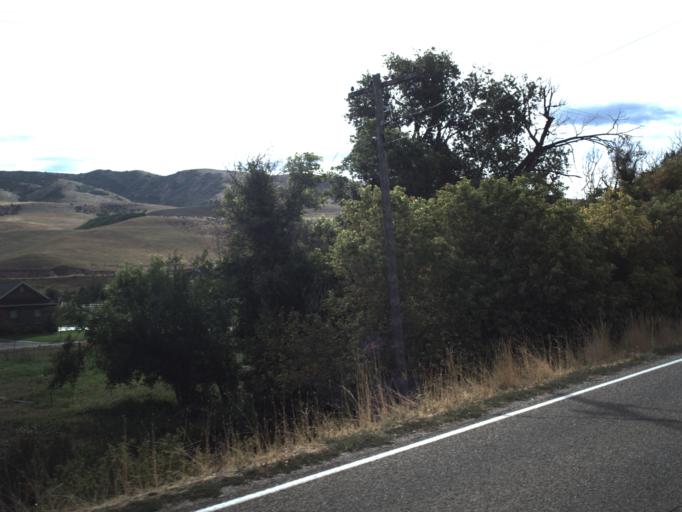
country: US
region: Utah
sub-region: Morgan County
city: Morgan
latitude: 40.9758
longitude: -111.6733
